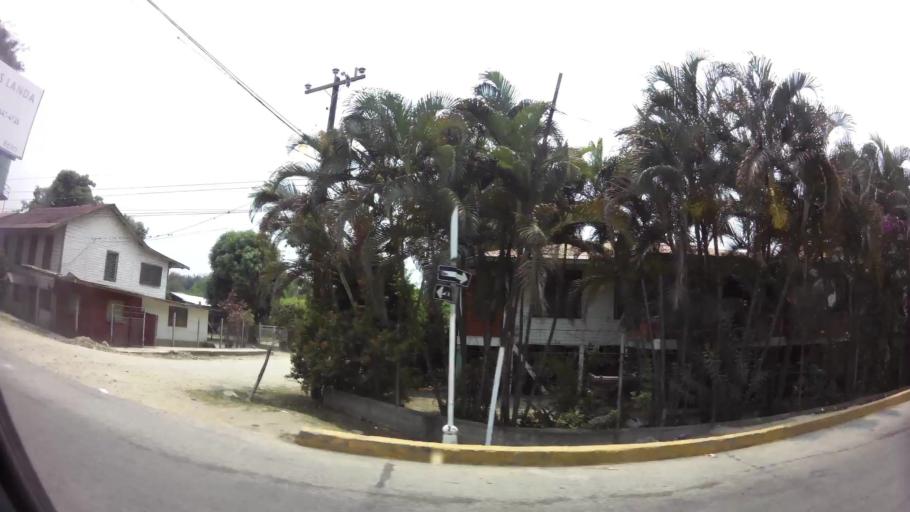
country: HN
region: Yoro
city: El Progreso
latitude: 15.3960
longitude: -87.8124
